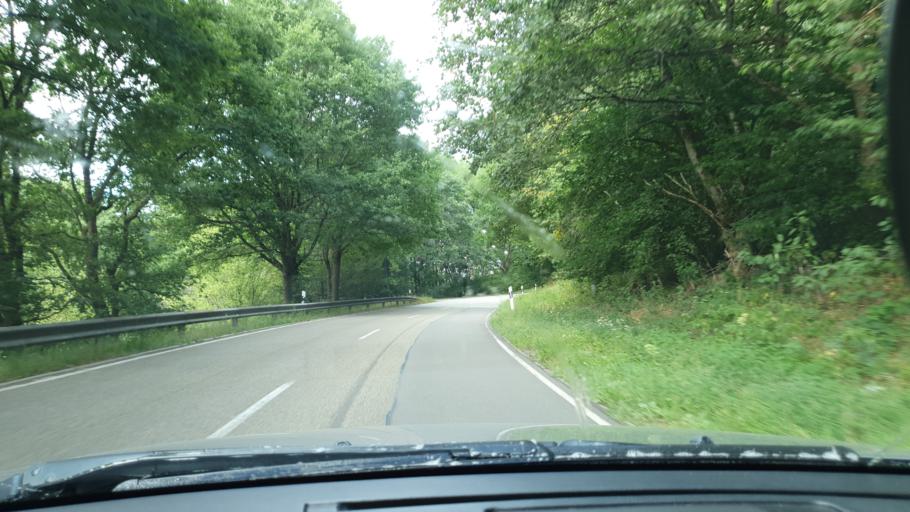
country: DE
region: Rheinland-Pfalz
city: Steinalben
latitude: 49.3194
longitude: 7.6484
